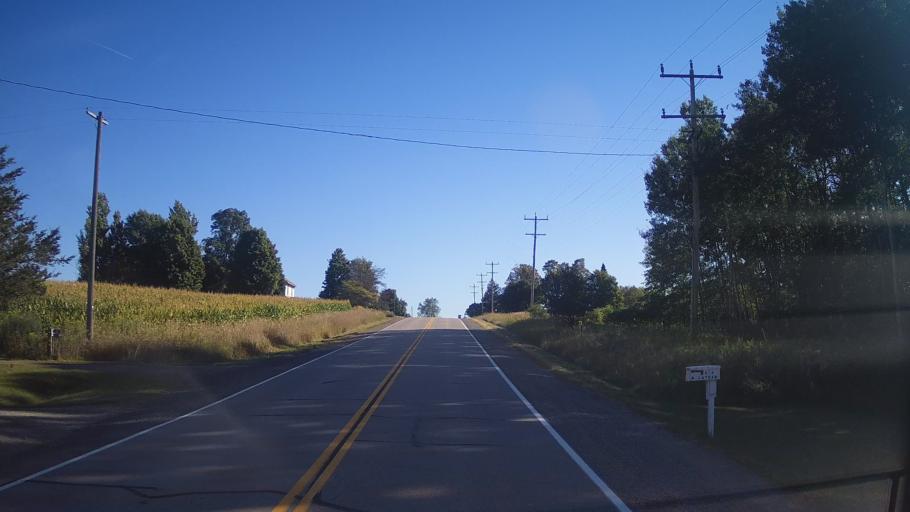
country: CA
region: Ontario
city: Gananoque
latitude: 44.5855
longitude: -76.1083
